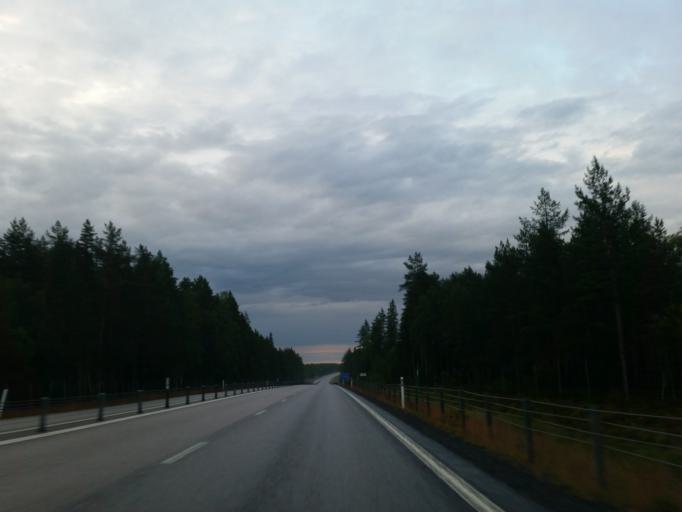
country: SE
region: Vaesterbotten
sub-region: Umea Kommun
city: Saevar
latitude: 63.9769
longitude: 20.7211
